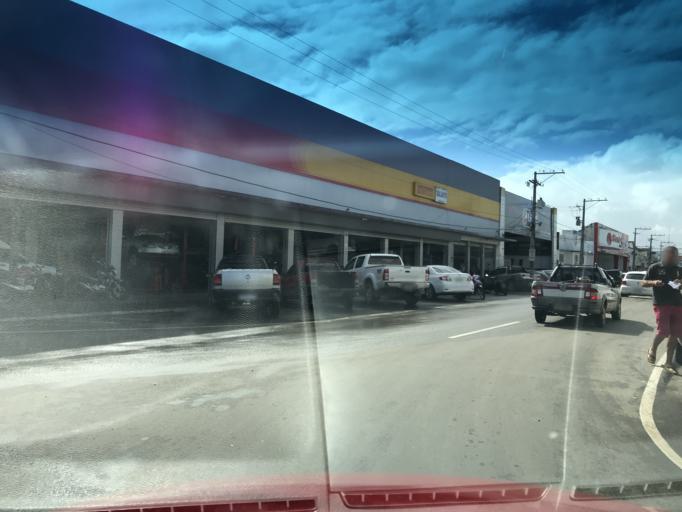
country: BR
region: Bahia
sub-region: Santo Antonio De Jesus
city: Santo Antonio de Jesus
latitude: -12.9659
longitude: -39.2721
